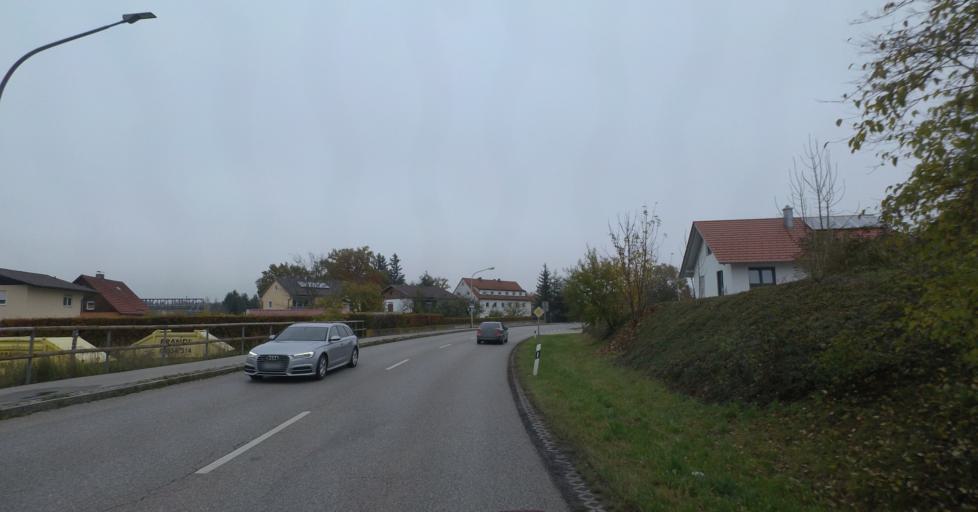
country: DE
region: Bavaria
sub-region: Upper Bavaria
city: Garching an der Alz
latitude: 48.1284
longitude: 12.5744
